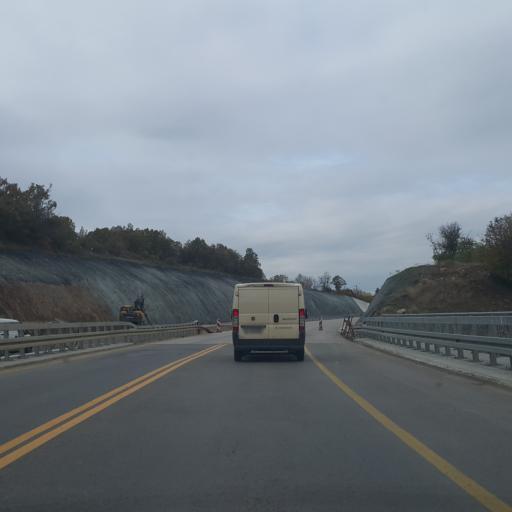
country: RS
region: Central Serbia
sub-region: Pirotski Okrug
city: Bela Palanka
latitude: 43.2194
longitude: 22.4116
